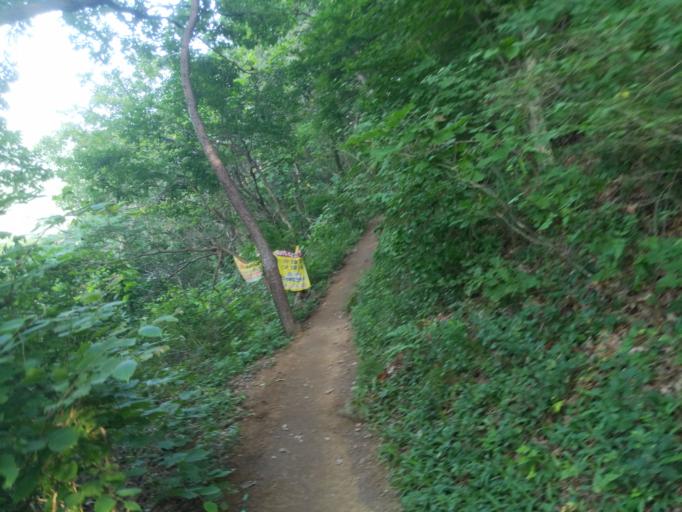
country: KR
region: Daegu
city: Hwawon
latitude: 35.7865
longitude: 128.5461
